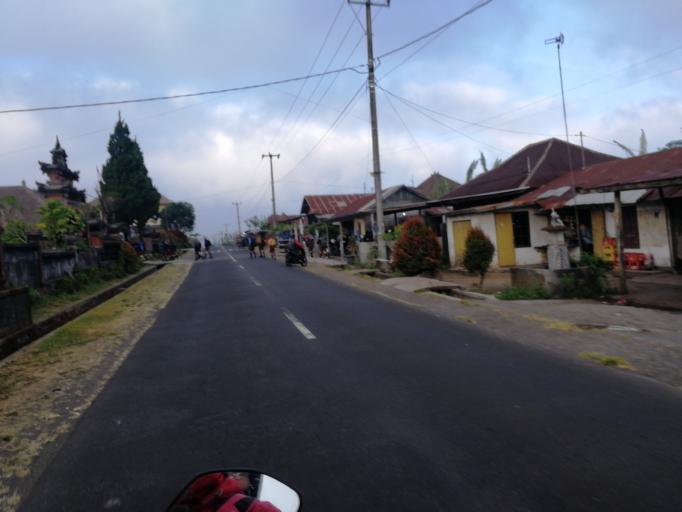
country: ID
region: Bali
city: Banjar Kedisan
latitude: -8.2220
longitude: 115.2658
